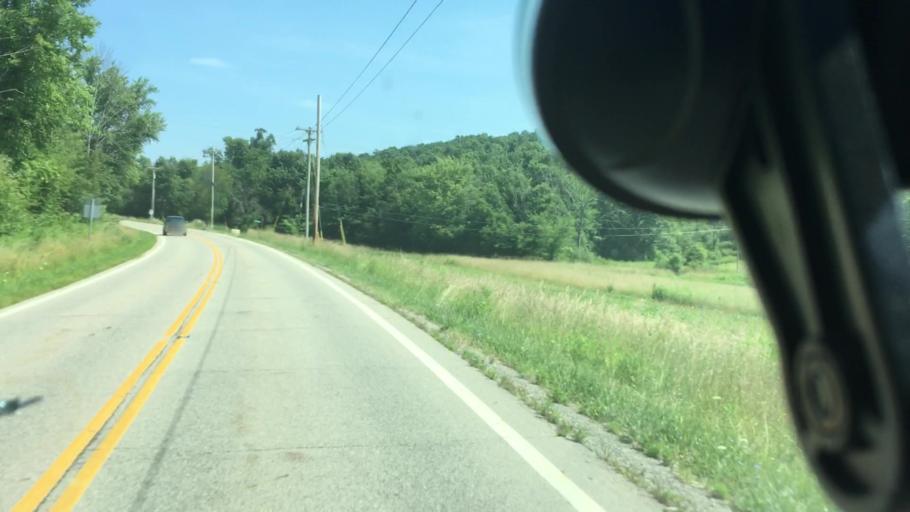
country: US
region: Ohio
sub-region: Columbiana County
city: Salineville
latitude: 40.6675
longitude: -80.8055
